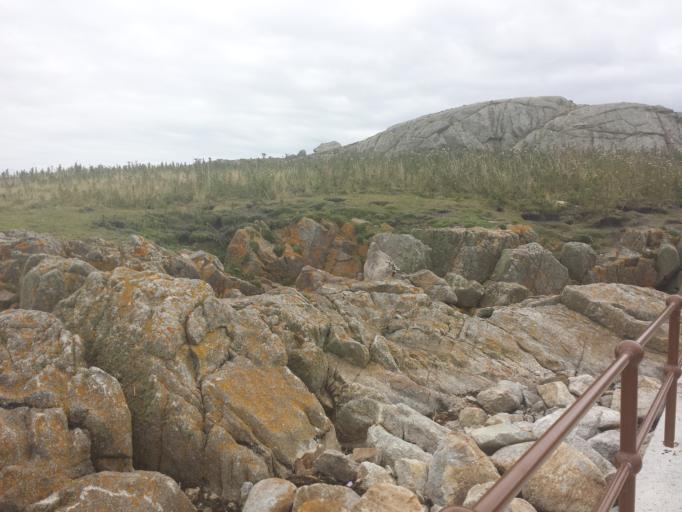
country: IE
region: Leinster
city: Dalkey
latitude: 53.2734
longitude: -6.0870
